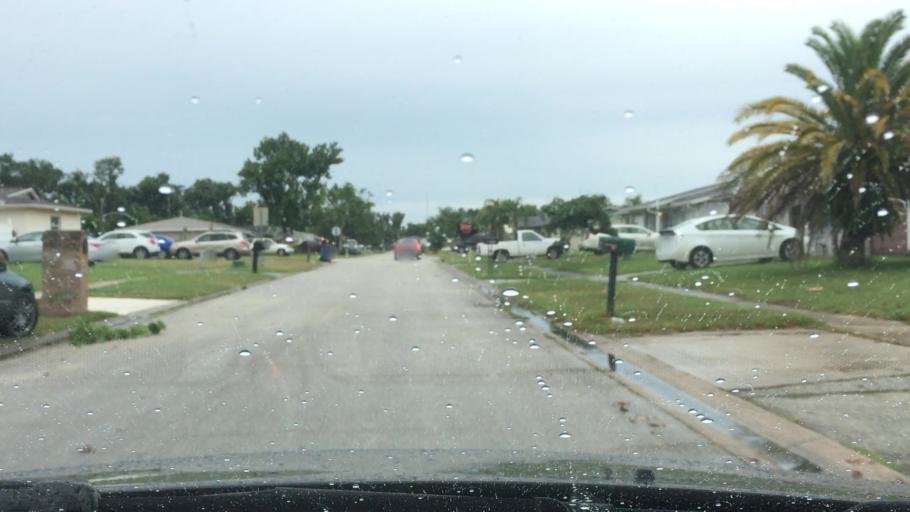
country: US
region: Florida
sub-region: Volusia County
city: Ormond Beach
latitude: 29.2523
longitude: -81.0758
